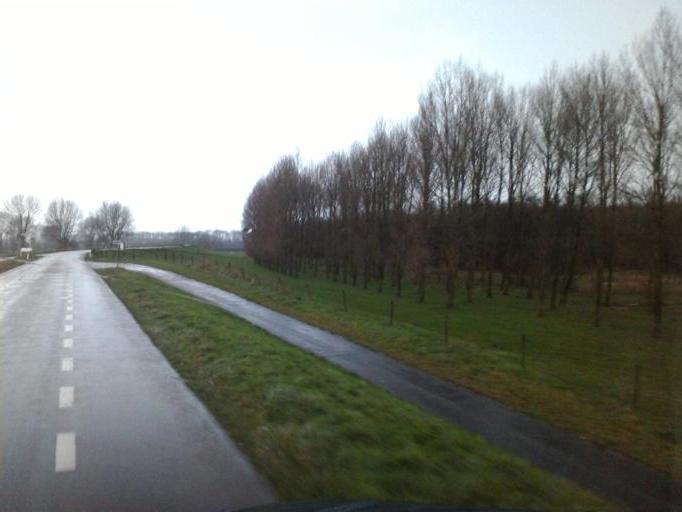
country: NL
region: Utrecht
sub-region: Gemeente Houten
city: Houten
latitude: 51.9935
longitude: 5.1459
